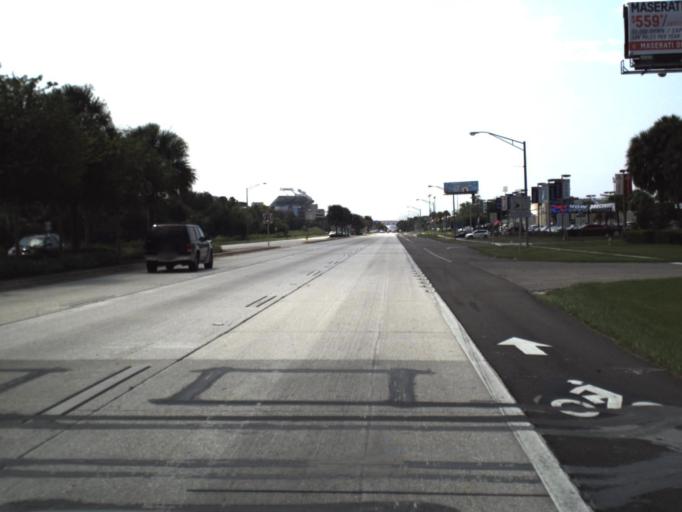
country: US
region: Florida
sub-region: Hillsborough County
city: Egypt Lake-Leto
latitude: 27.9874
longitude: -82.5054
